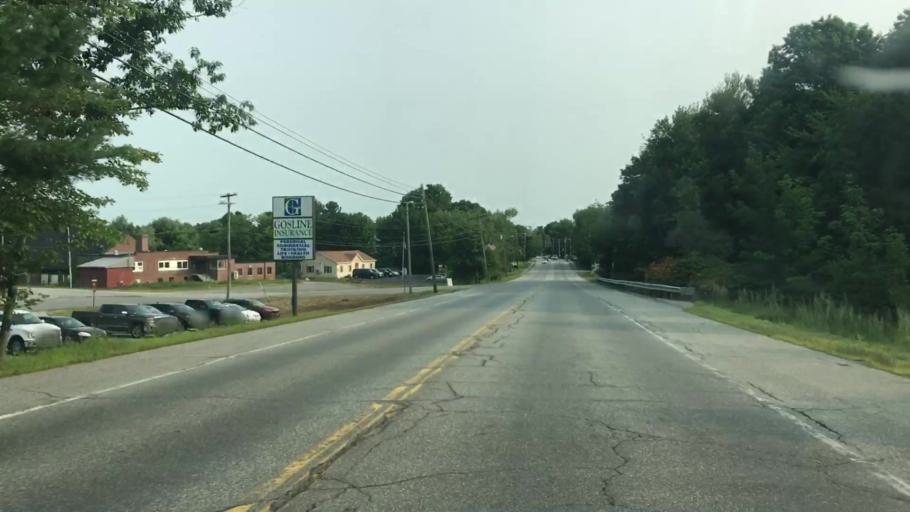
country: US
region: Maine
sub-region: Kennebec County
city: Gardiner
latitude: 44.2147
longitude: -69.7827
